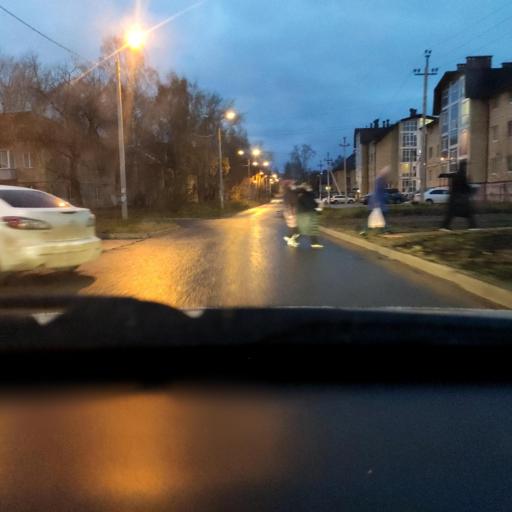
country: RU
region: Perm
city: Kondratovo
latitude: 58.0391
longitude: 56.1124
